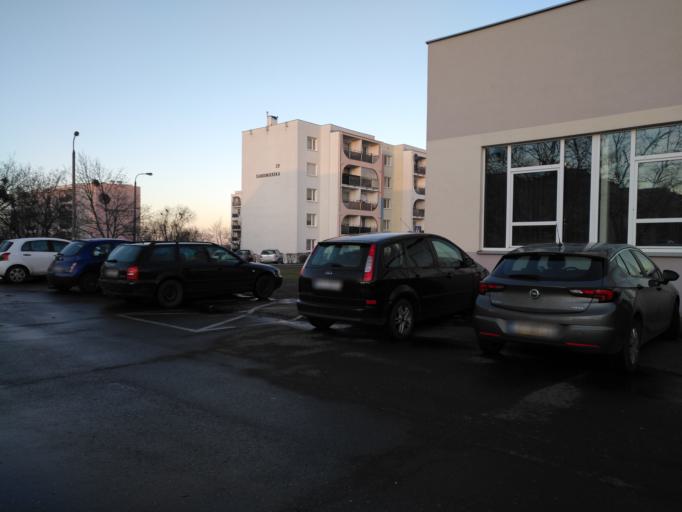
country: PL
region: Kujawsko-Pomorskie
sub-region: Bydgoszcz
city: Bydgoszcz
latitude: 53.1103
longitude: 18.0586
